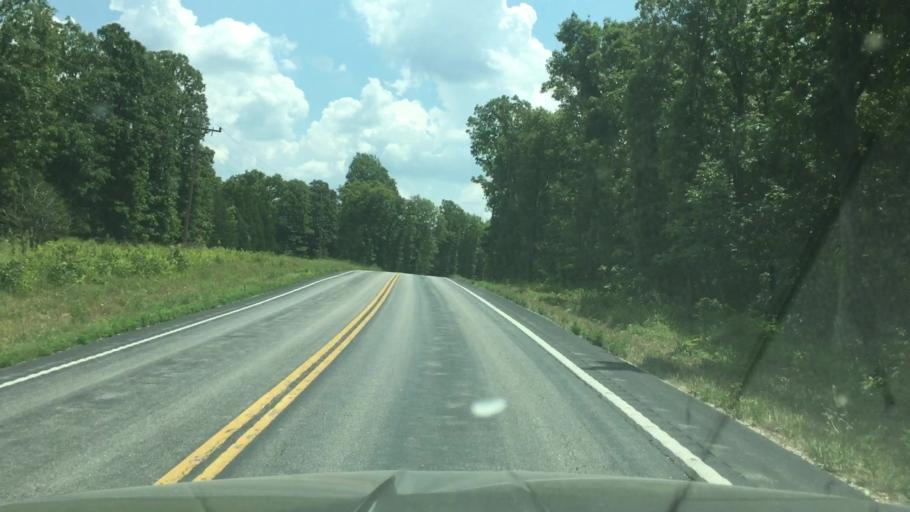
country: US
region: Missouri
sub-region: Camden County
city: Osage Beach
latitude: 38.1352
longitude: -92.5699
